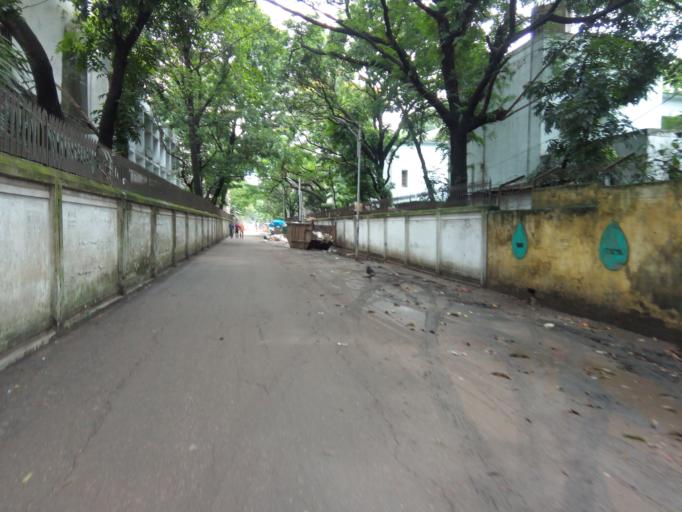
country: BD
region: Dhaka
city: Azimpur
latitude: 23.7356
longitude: 90.3808
